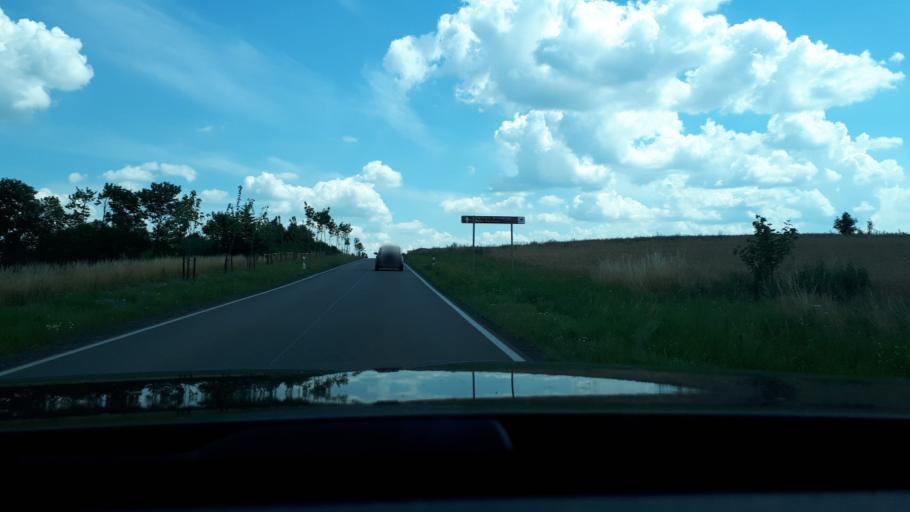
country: PL
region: Warmian-Masurian Voivodeship
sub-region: Powiat olsztynski
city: Olsztynek
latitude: 53.5841
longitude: 20.3053
